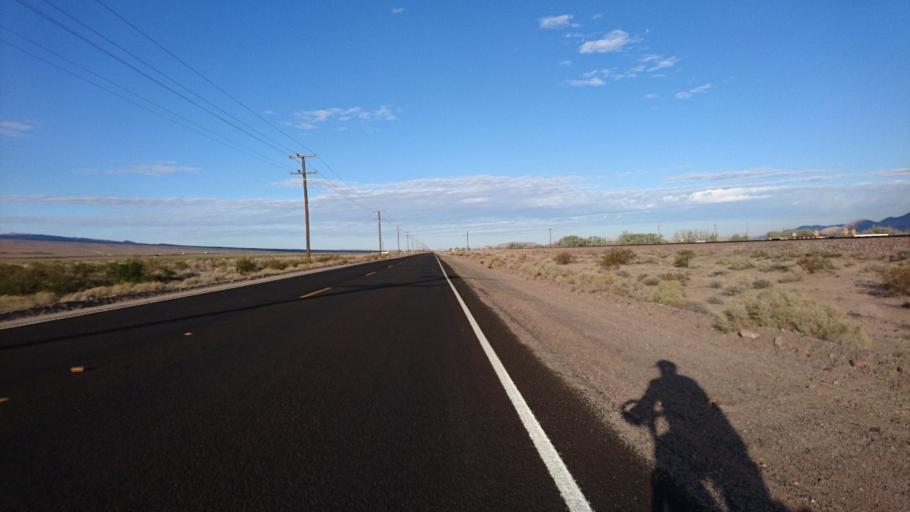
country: US
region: California
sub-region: San Bernardino County
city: Barstow
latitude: 34.8386
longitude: -116.7298
